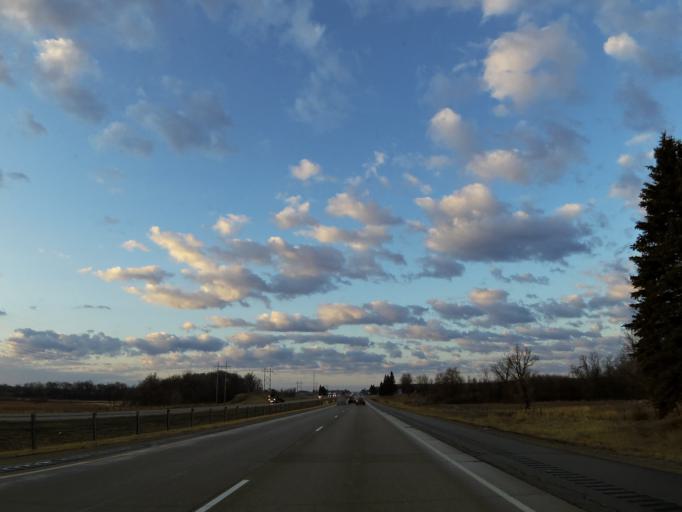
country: US
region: Minnesota
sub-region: Rice County
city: Dundas
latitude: 44.4219
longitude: -93.2928
